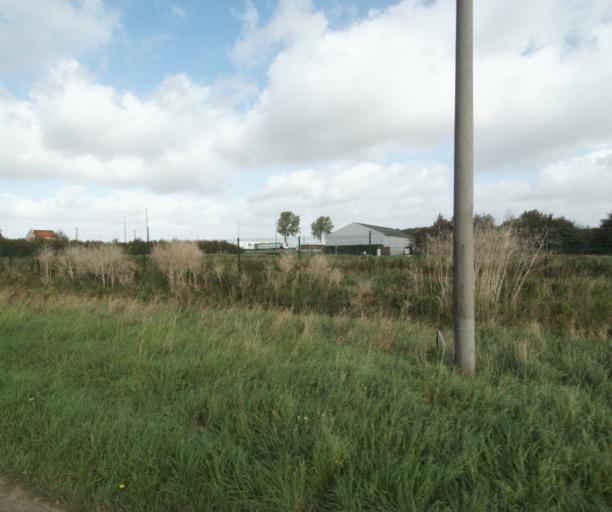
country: FR
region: Nord-Pas-de-Calais
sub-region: Departement du Nord
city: Fournes-en-Weppes
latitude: 50.5782
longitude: 2.8752
